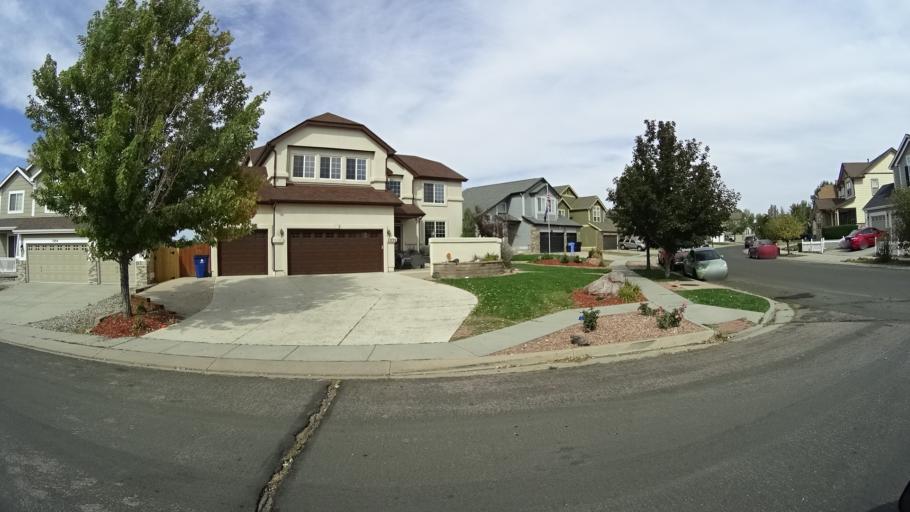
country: US
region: Colorado
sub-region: El Paso County
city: Cimarron Hills
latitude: 38.9111
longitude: -104.6986
